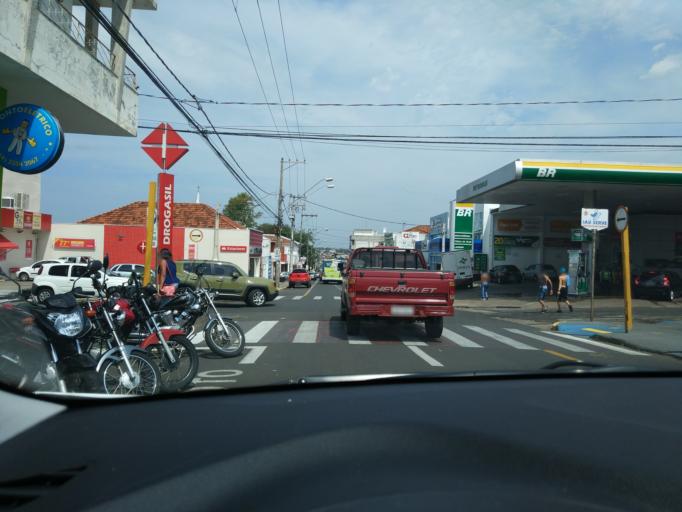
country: BR
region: Sao Paulo
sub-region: Botucatu
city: Botucatu
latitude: -22.8702
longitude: -48.4488
